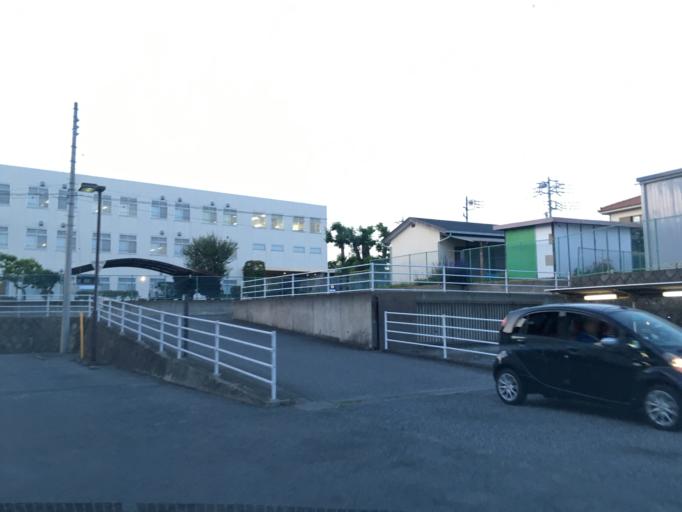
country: JP
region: Saitama
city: Sayama
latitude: 35.8447
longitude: 139.3753
